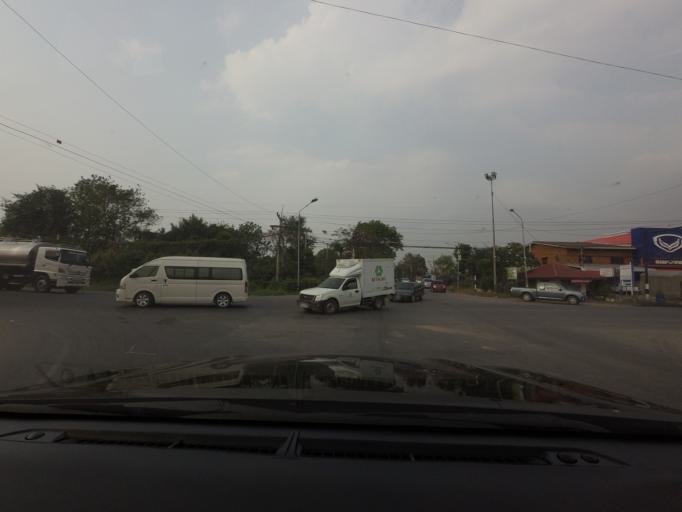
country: TH
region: Sara Buri
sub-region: Amphoe Wang Muang
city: Wang Muang
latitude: 14.8427
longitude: 101.1140
